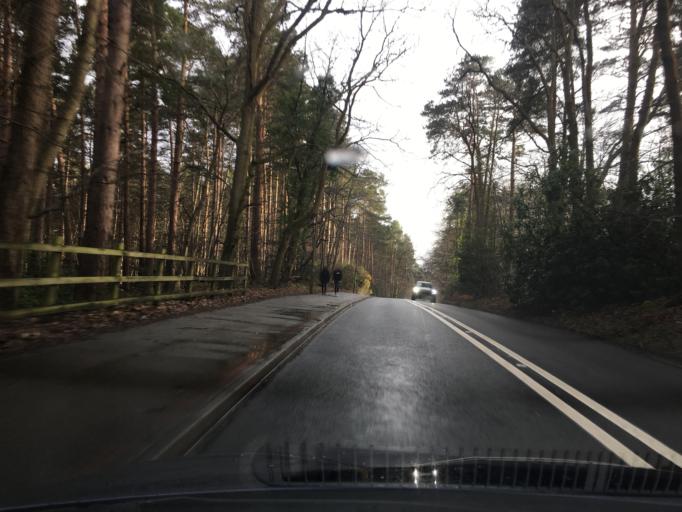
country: GB
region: England
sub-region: Bracknell Forest
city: Crowthorne
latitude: 51.3585
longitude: -0.7984
